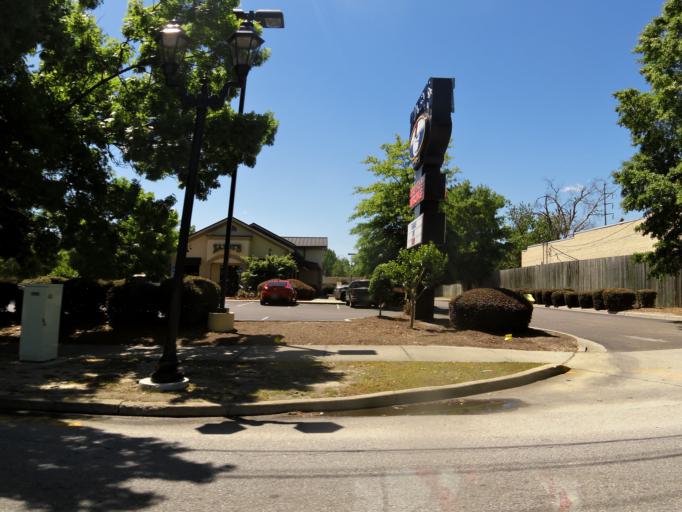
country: US
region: Georgia
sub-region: Richmond County
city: Augusta
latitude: 33.4755
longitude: -81.9957
